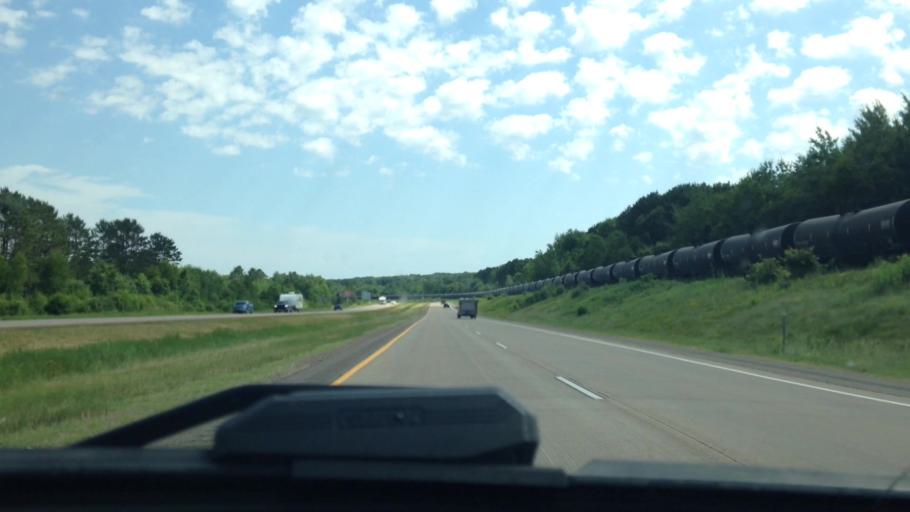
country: US
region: Wisconsin
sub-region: Washburn County
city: Spooner
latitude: 45.8609
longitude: -91.8427
